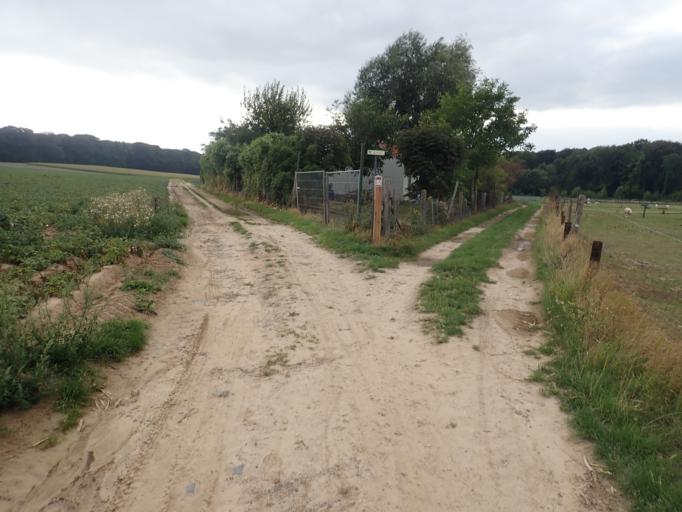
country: BE
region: Flanders
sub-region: Provincie Vlaams-Brabant
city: Asse
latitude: 50.9324
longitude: 4.2077
